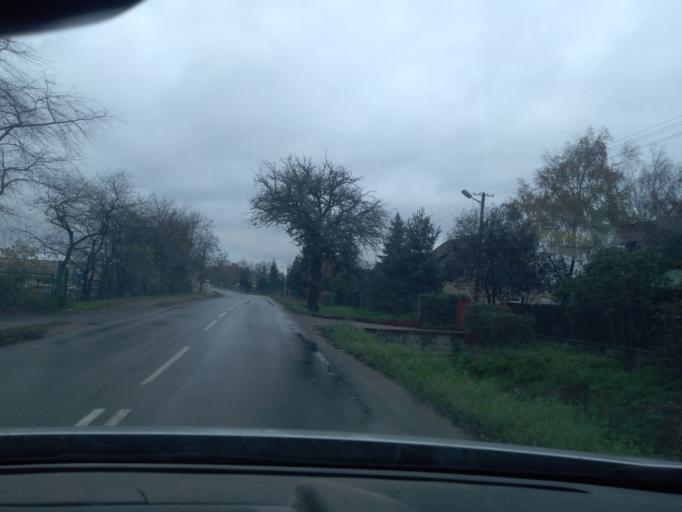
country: PL
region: Greater Poland Voivodeship
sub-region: Powiat obornicki
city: Oborniki
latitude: 52.6587
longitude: 16.8409
